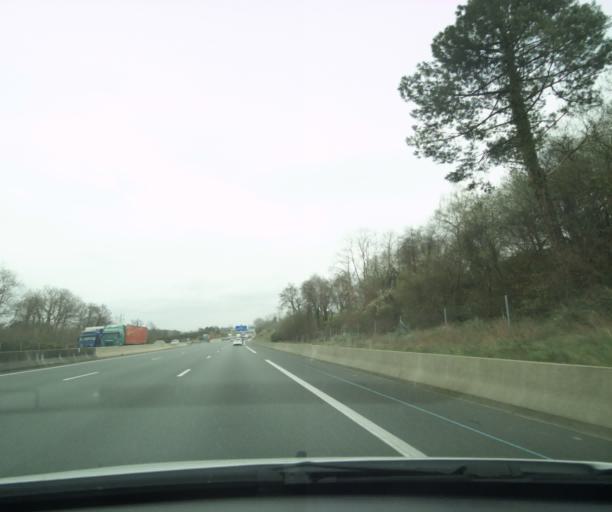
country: FR
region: Aquitaine
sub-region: Departement des Pyrenees-Atlantiques
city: Anglet
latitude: 43.4614
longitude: -1.5085
